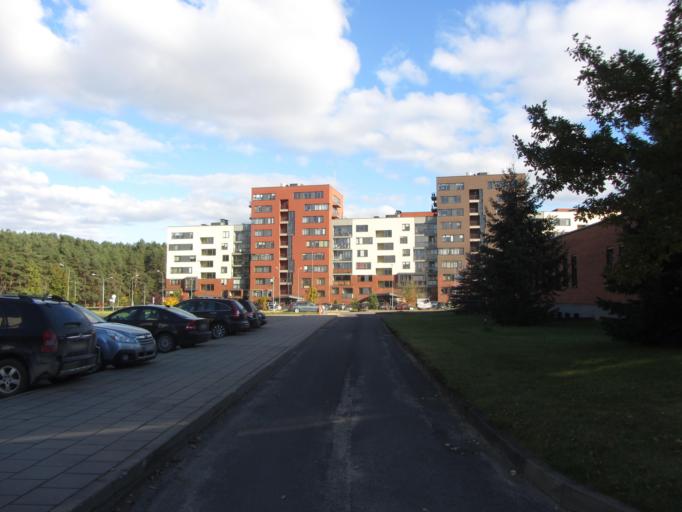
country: LT
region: Vilnius County
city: Lazdynai
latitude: 54.6685
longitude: 25.2086
